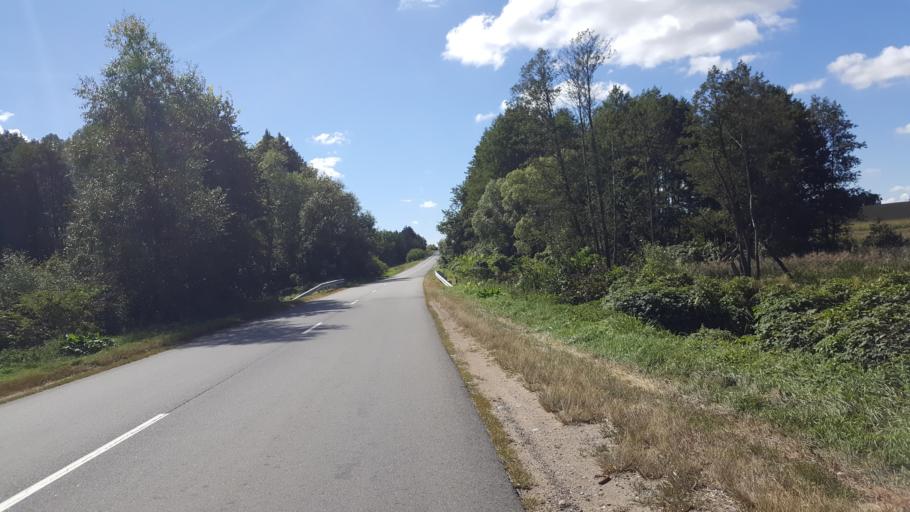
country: BY
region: Brest
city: Vysokaye
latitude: 52.2959
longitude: 23.3053
